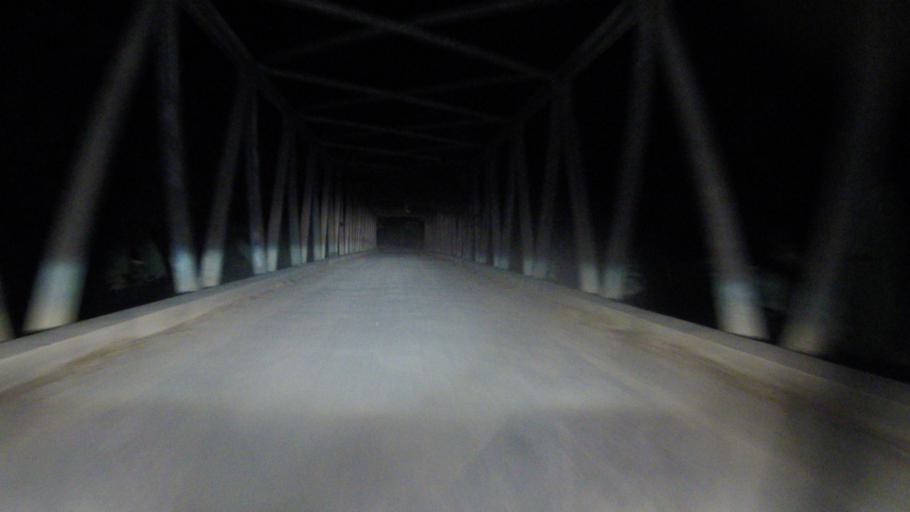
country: TL
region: Viqueque
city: Viqueque
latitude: -8.8329
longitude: 126.5202
